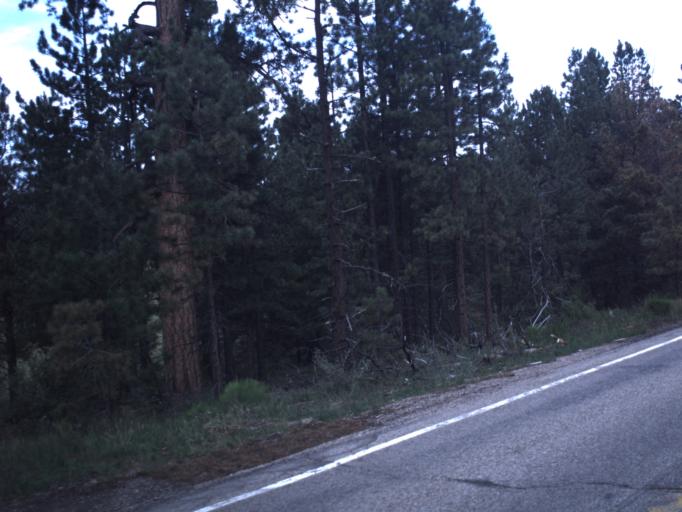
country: US
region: Utah
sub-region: Garfield County
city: Panguitch
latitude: 37.5000
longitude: -112.6223
